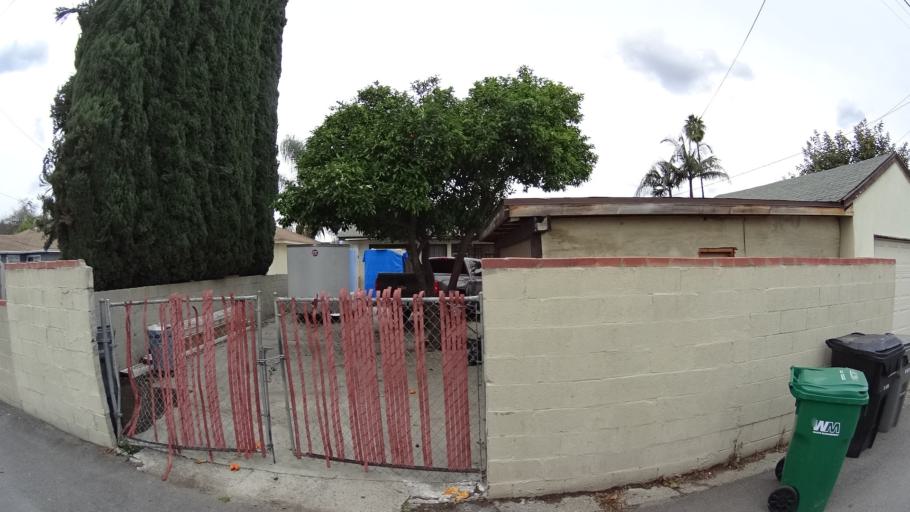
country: US
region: California
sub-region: Los Angeles County
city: Baldwin Park
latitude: 34.0818
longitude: -117.9488
